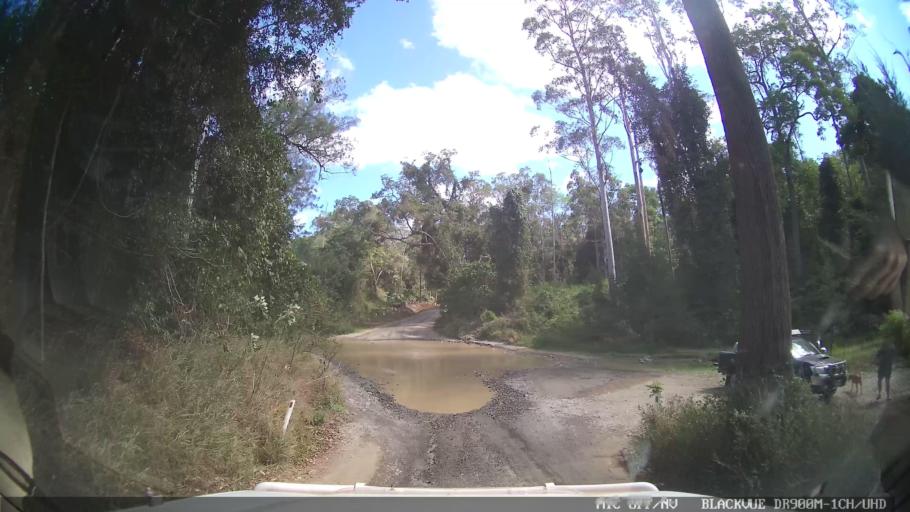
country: AU
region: Queensland
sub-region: Sunshine Coast
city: Nambour
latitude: -26.6319
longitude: 152.6523
